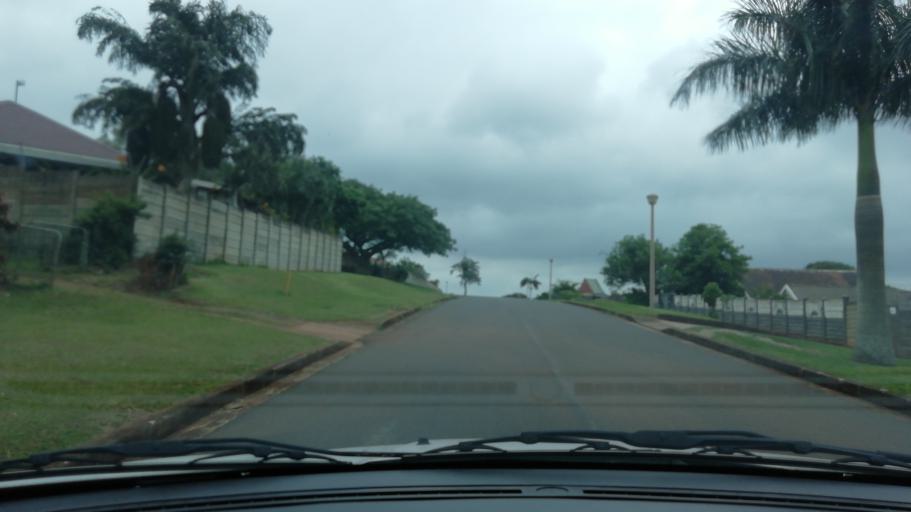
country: ZA
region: KwaZulu-Natal
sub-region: uThungulu District Municipality
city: Empangeni
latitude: -28.7632
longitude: 31.9041
